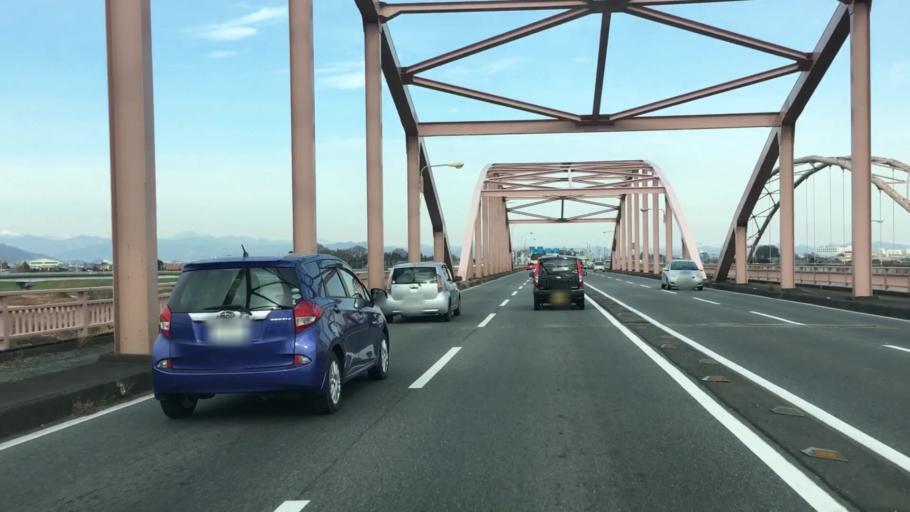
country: JP
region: Saitama
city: Menuma
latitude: 36.2399
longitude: 139.3787
